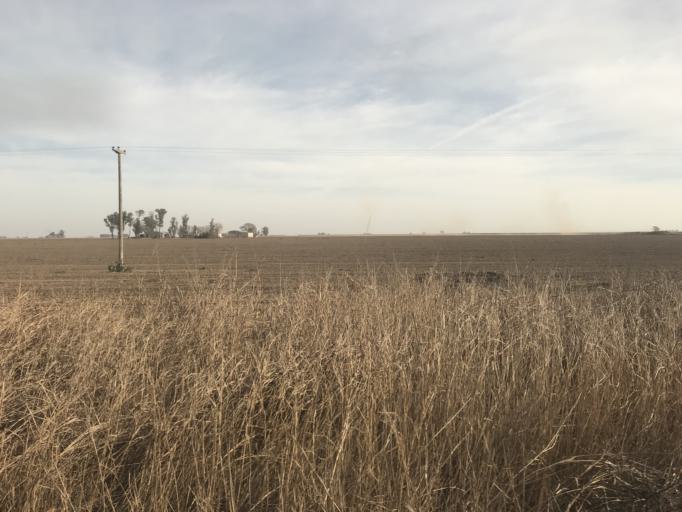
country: AR
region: Cordoba
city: Laguna Larga
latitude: -31.7494
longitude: -63.8271
